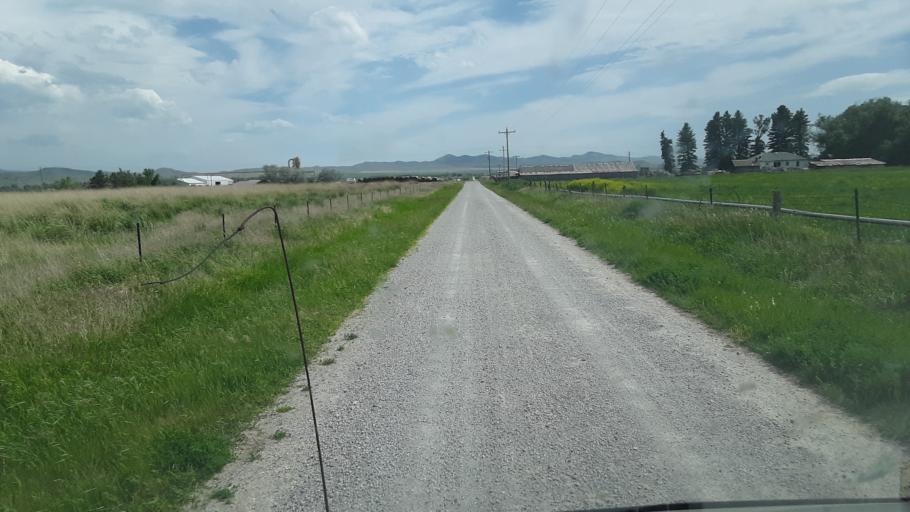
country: US
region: Montana
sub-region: Broadwater County
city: Townsend
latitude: 46.1756
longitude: -111.4719
